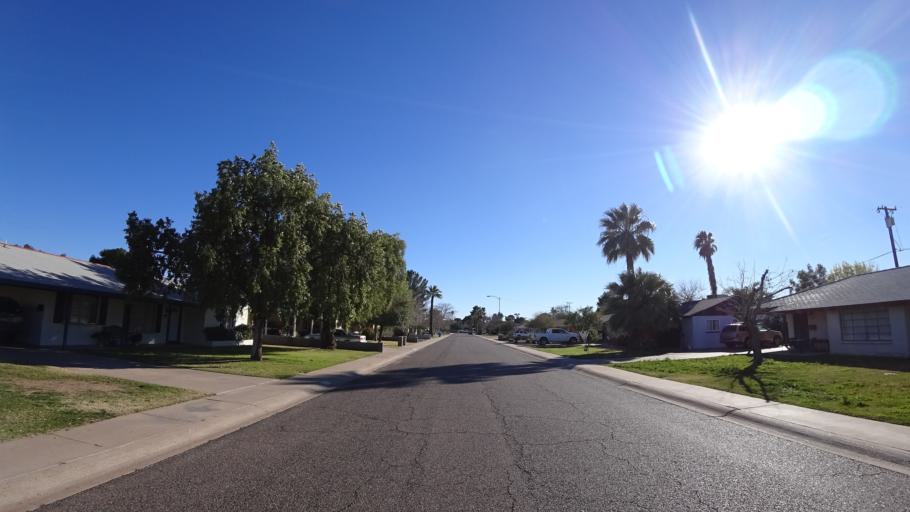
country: US
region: Arizona
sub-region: Maricopa County
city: Phoenix
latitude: 33.5222
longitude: -112.0537
